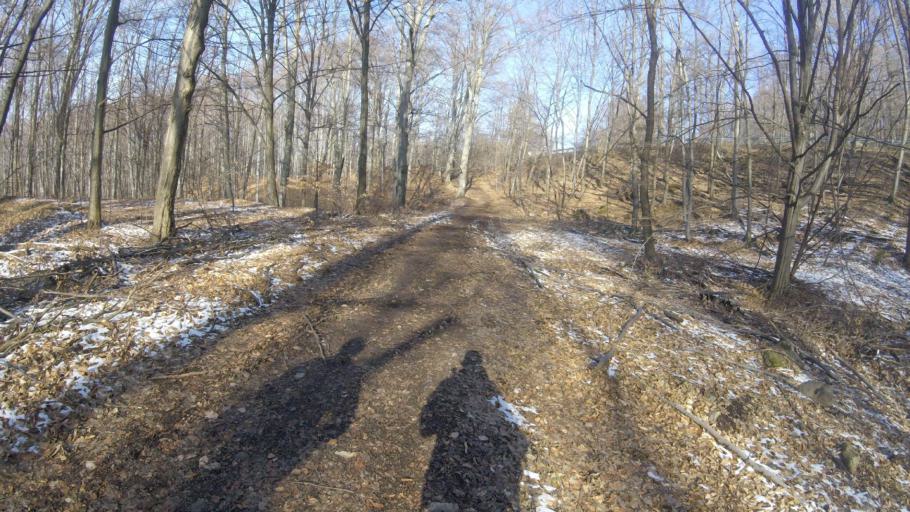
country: HU
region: Heves
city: Paradsasvar
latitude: 47.8765
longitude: 19.9796
